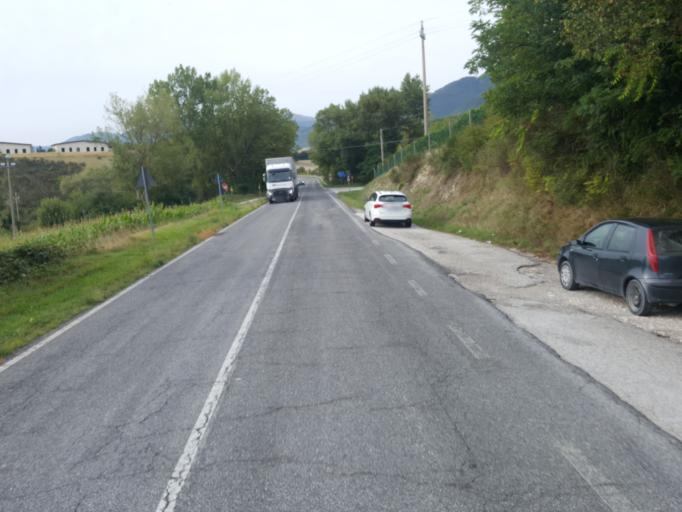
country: IT
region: The Marches
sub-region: Provincia di Ancona
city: Fabriano
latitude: 43.3470
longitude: 12.8296
